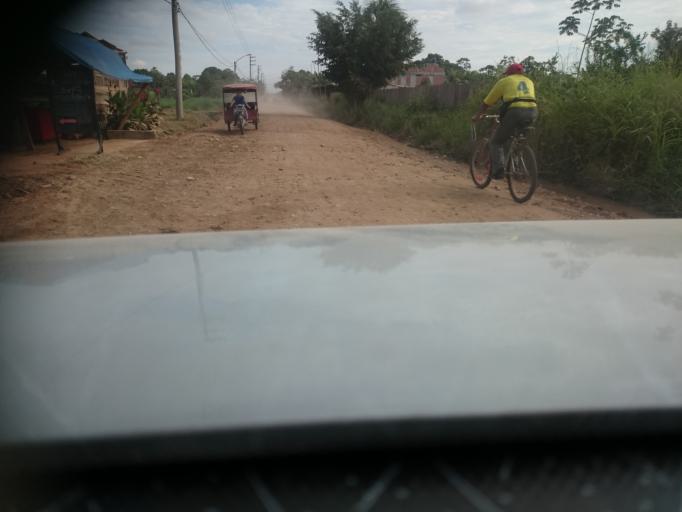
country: PE
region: Ucayali
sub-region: Provincia de Coronel Portillo
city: Puerto Callao
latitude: -8.3853
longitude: -74.5961
